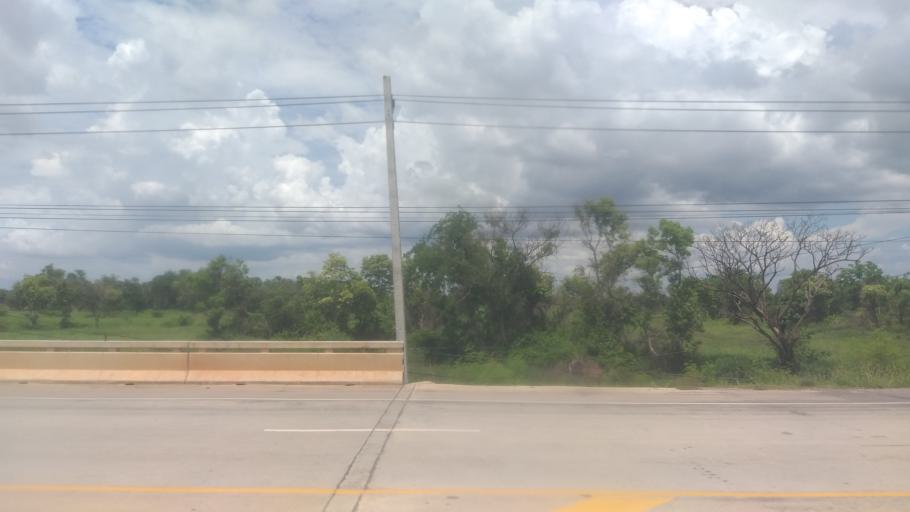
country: TH
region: Nakhon Ratchasima
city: Non Thai
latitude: 15.1293
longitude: 102.1037
